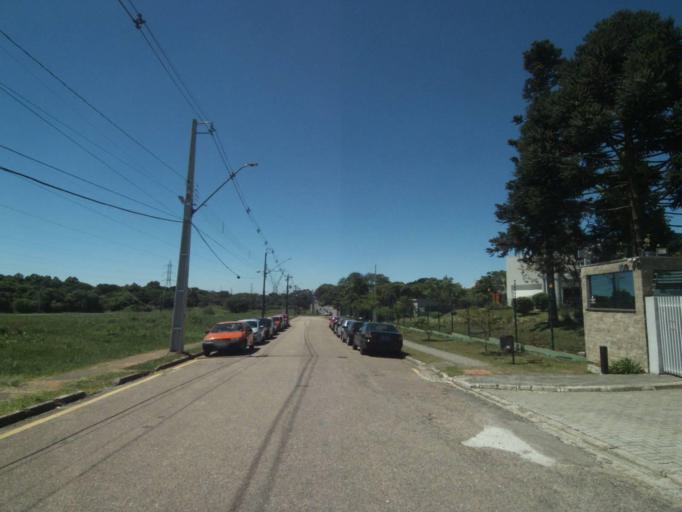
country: BR
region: Parana
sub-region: Curitiba
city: Curitiba
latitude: -25.4704
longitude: -49.3476
